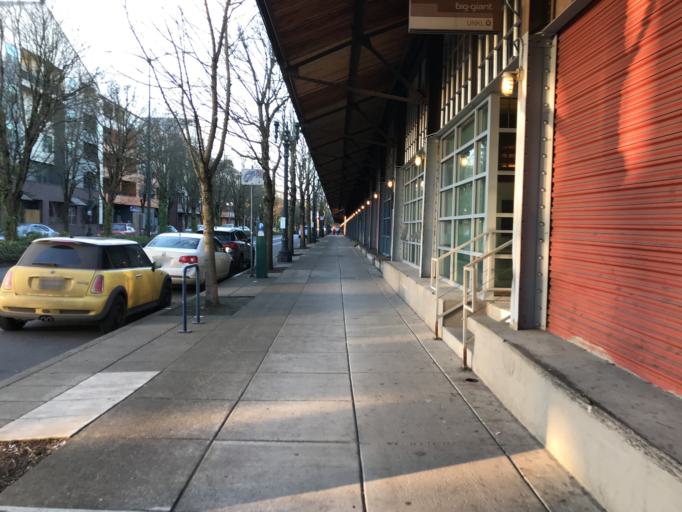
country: US
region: Oregon
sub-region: Multnomah County
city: Portland
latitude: 45.5282
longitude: -122.6732
